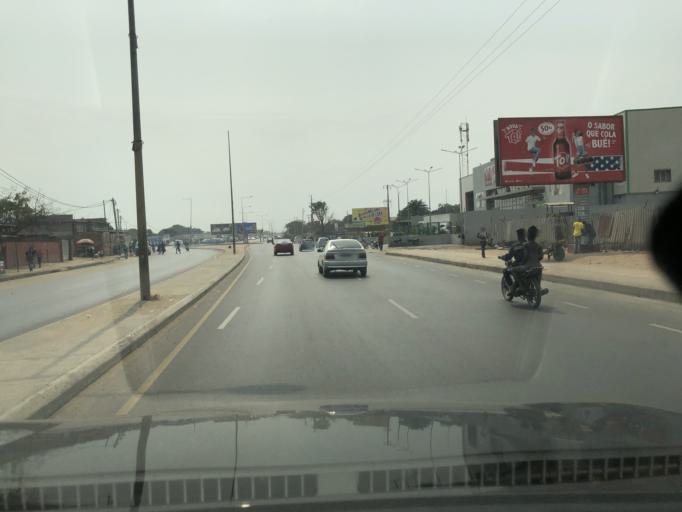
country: AO
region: Luanda
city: Luanda
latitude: -8.7997
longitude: 13.3139
